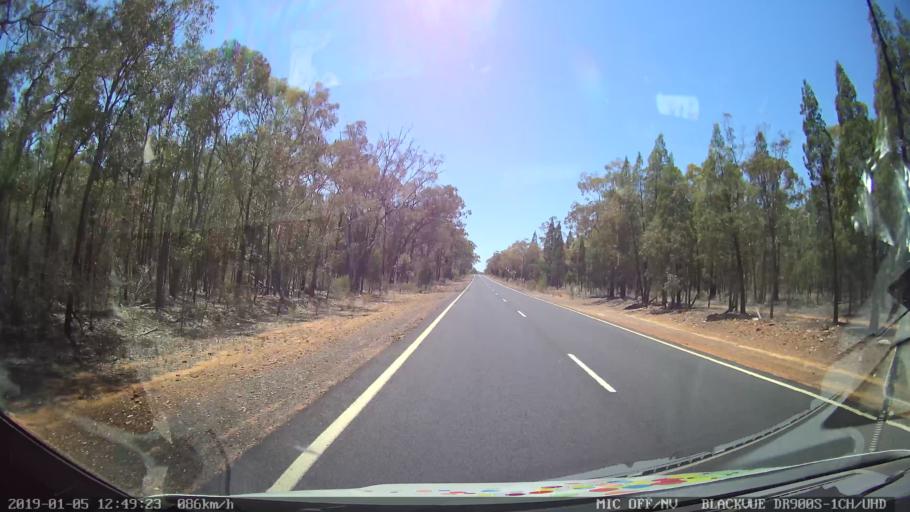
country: AU
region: New South Wales
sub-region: Warrumbungle Shire
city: Coonabarabran
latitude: -31.1177
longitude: 149.6064
